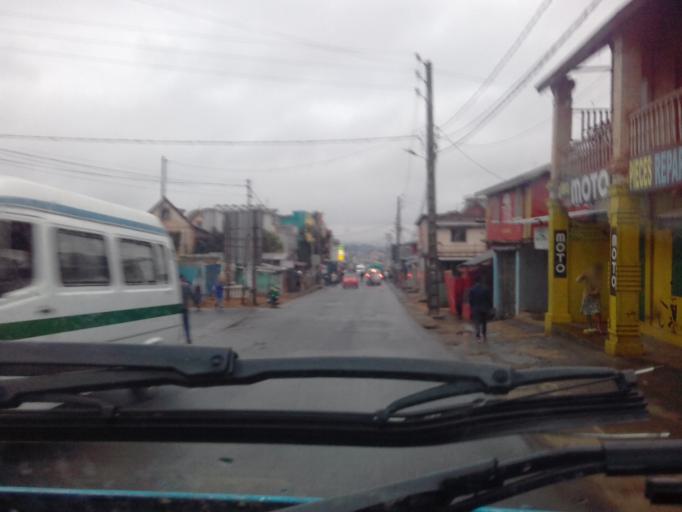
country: MG
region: Analamanga
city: Antananarivo
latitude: -18.8755
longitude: 47.5482
